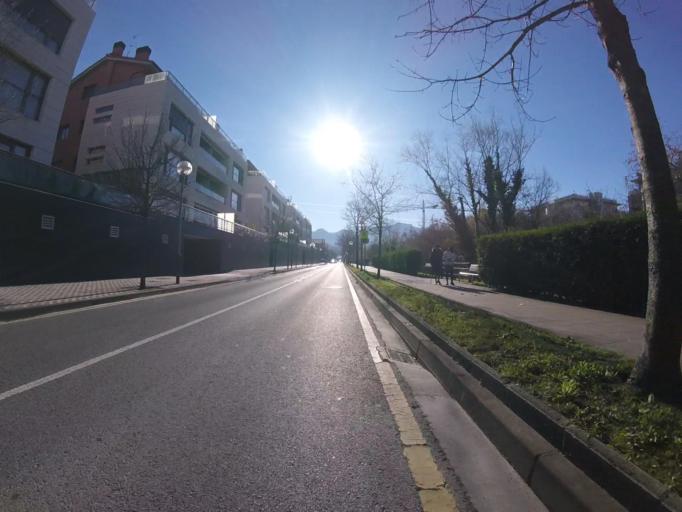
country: ES
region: Basque Country
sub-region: Provincia de Guipuzcoa
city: Irun
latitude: 43.3389
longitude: -1.7781
